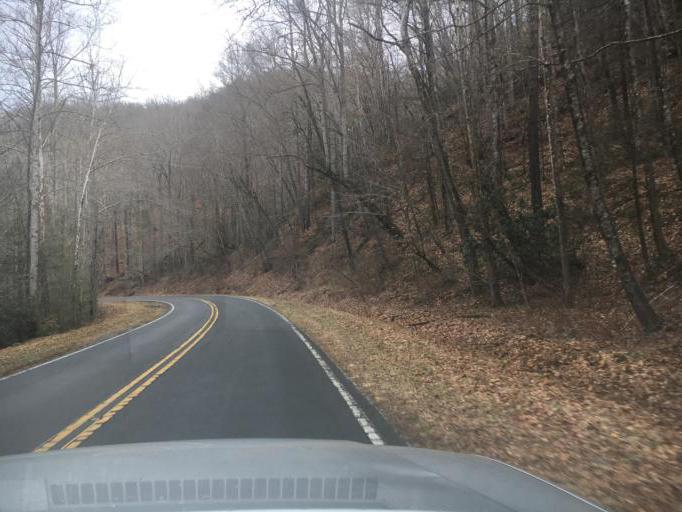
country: US
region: North Carolina
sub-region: Transylvania County
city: Brevard
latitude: 35.2871
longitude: -82.7612
